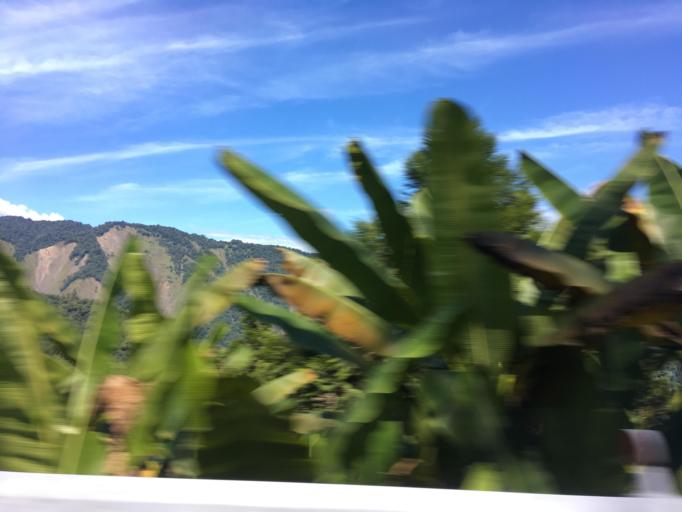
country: TW
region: Taiwan
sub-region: Yilan
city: Yilan
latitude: 24.5394
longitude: 121.5118
